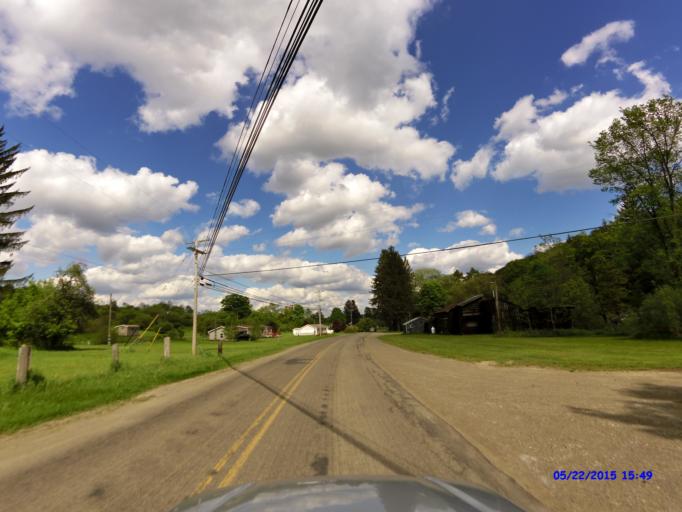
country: US
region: New York
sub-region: Cattaraugus County
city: Franklinville
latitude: 42.3374
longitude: -78.4828
